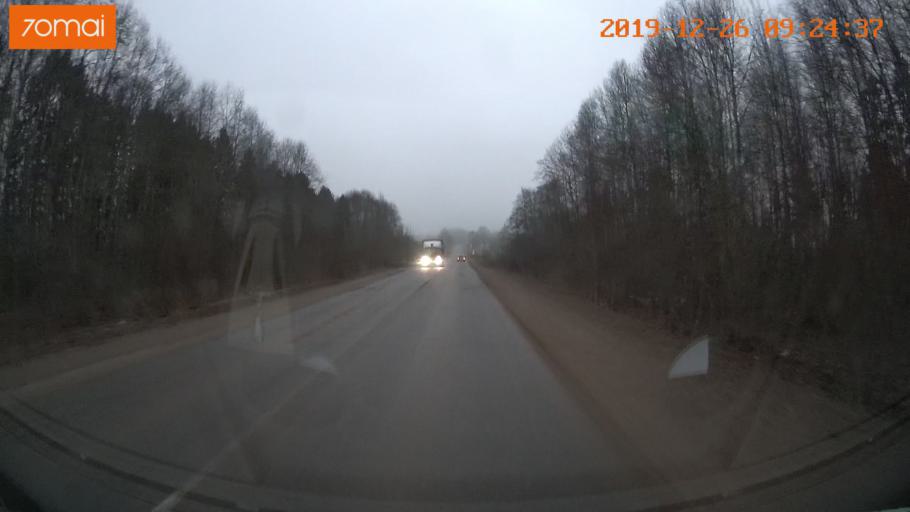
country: RU
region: Vologda
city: Gryazovets
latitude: 59.0028
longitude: 40.1968
